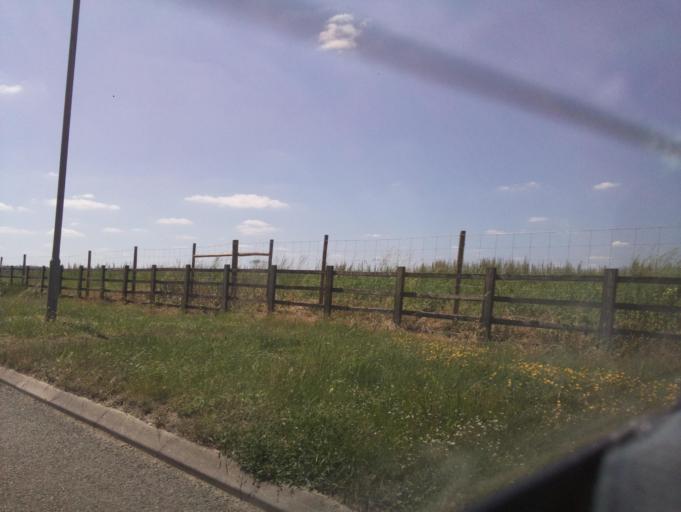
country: GB
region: England
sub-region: Wiltshire
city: Calne
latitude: 51.4456
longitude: -2.0187
